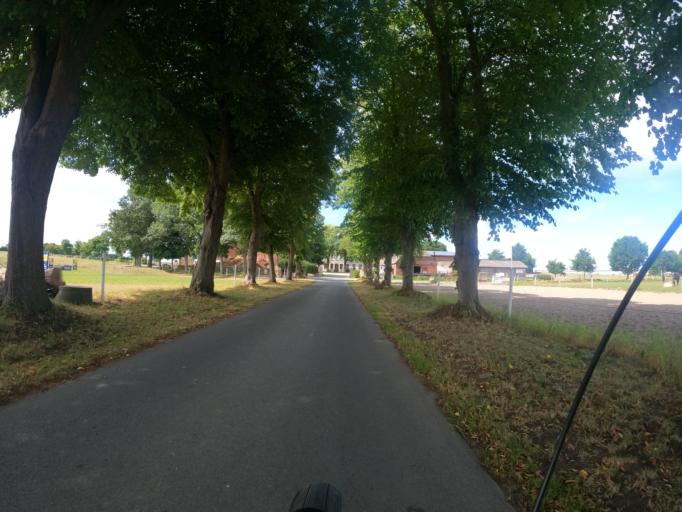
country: DE
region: Schleswig-Holstein
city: Steinbergkirche
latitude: 54.7696
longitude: 9.7616
